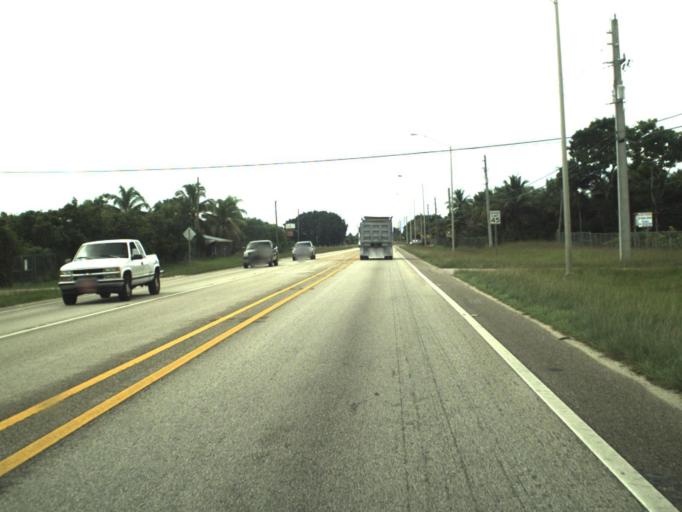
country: US
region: Florida
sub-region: Miami-Dade County
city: Richmond West
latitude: 25.6081
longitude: -80.4790
